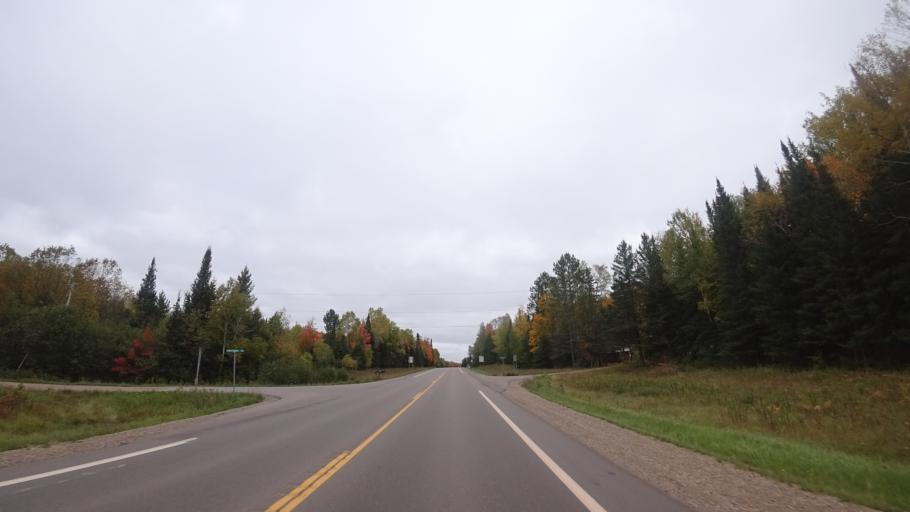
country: US
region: Michigan
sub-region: Iron County
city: Crystal Falls
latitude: 46.1596
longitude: -88.0803
